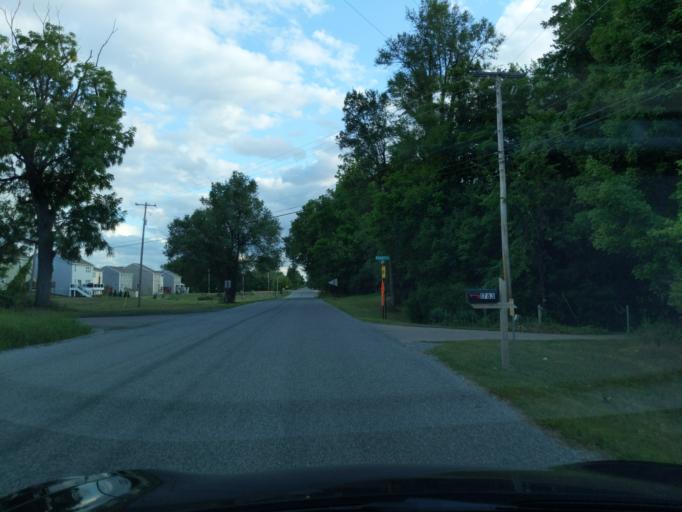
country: US
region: Michigan
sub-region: Eaton County
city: Dimondale
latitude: 42.6332
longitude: -84.5824
